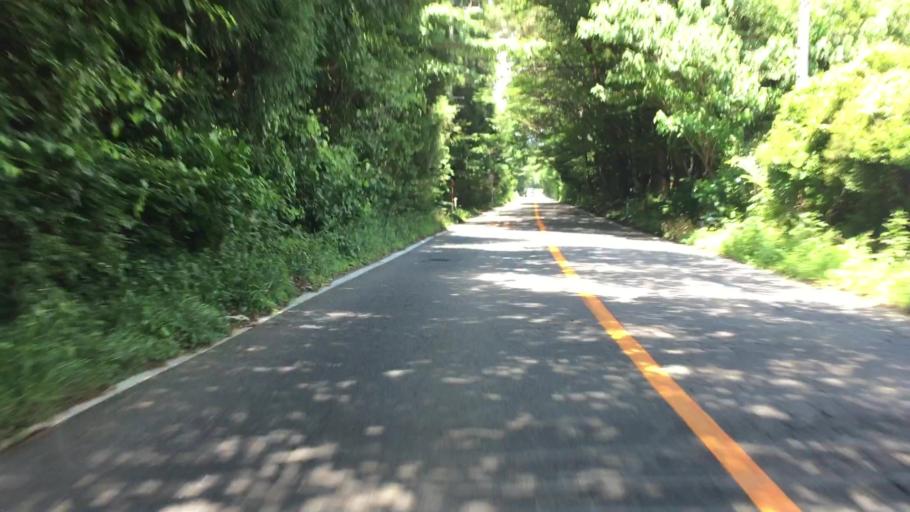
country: JP
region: Tochigi
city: Kuroiso
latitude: 37.0207
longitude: 139.9502
